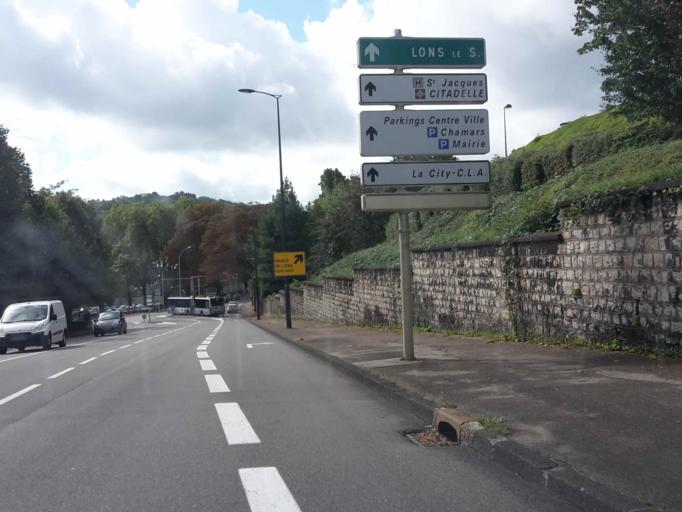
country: FR
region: Franche-Comte
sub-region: Departement du Doubs
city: Besancon
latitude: 47.2390
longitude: 6.0148
